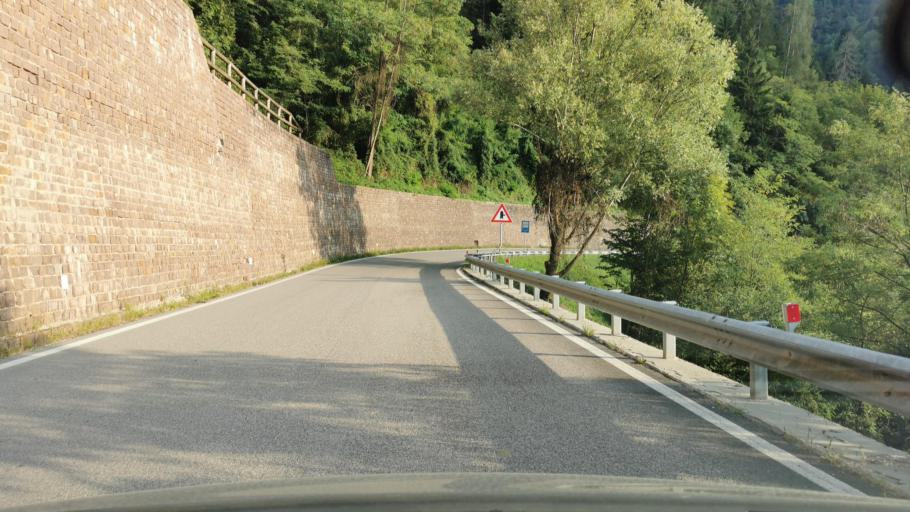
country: IT
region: Trentino-Alto Adige
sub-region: Provincia di Trento
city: Frassilongo
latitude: 46.0779
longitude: 11.2829
